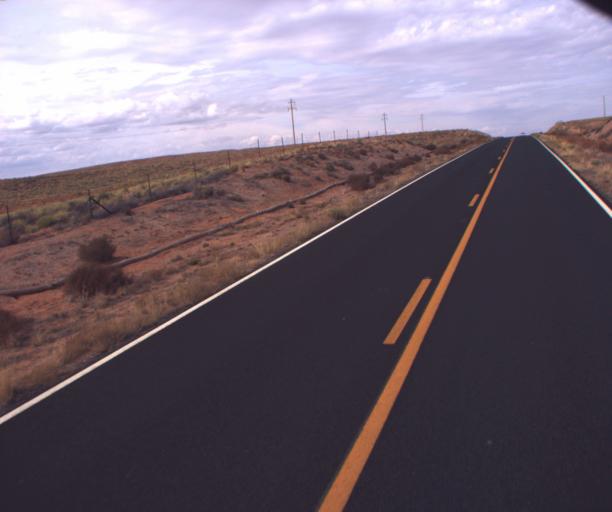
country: US
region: Arizona
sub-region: Apache County
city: Many Farms
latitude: 36.5979
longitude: -109.5674
